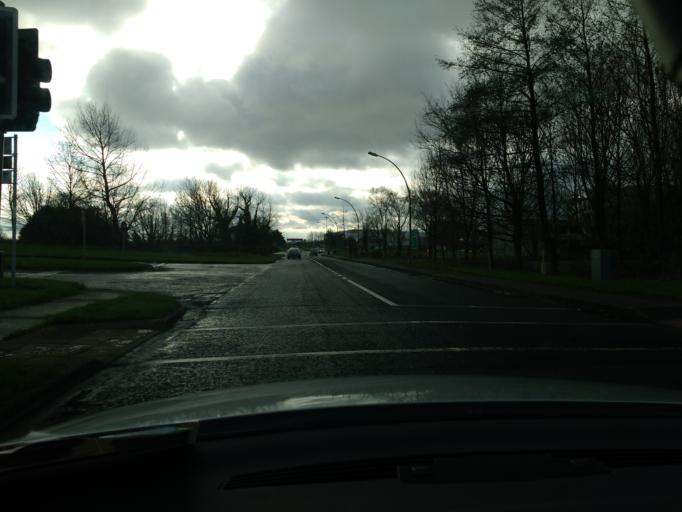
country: IE
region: Munster
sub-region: An Clar
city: Shannon
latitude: 52.6990
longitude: -8.8998
